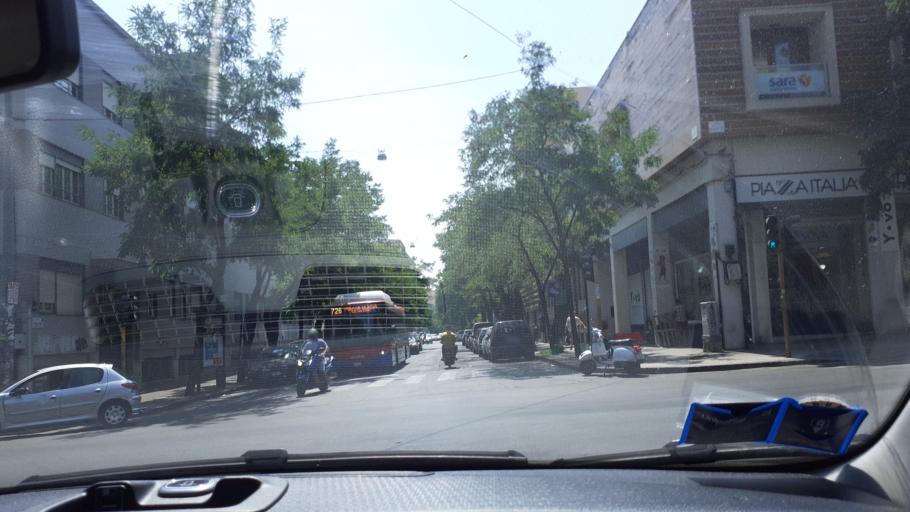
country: IT
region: Sicily
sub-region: Catania
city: Catania
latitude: 37.5118
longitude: 15.0748
